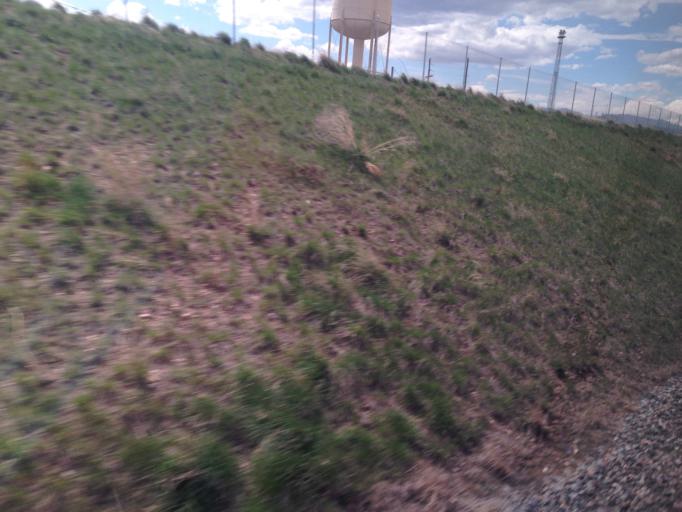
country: US
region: Colorado
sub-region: Adams County
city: Twin Lakes
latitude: 39.8037
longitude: -105.0025
